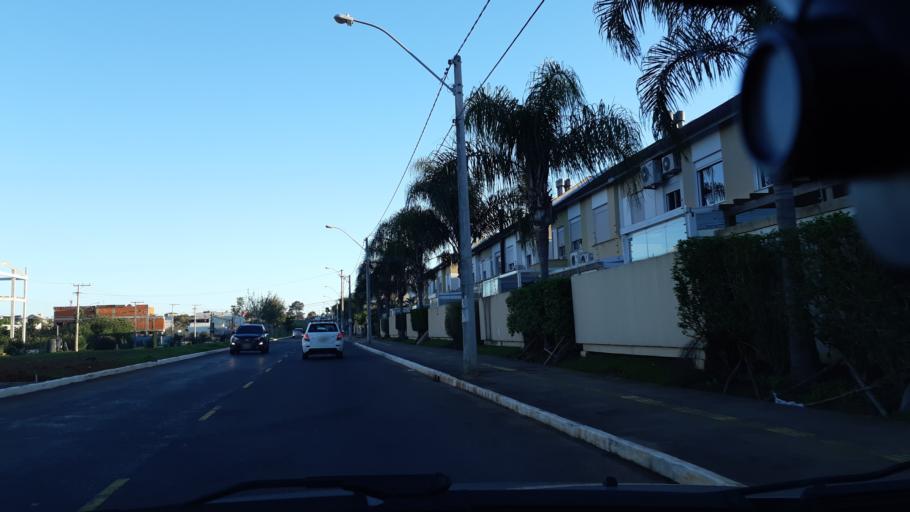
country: BR
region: Rio Grande do Sul
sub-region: Canoas
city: Canoas
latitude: -29.9221
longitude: -51.1556
